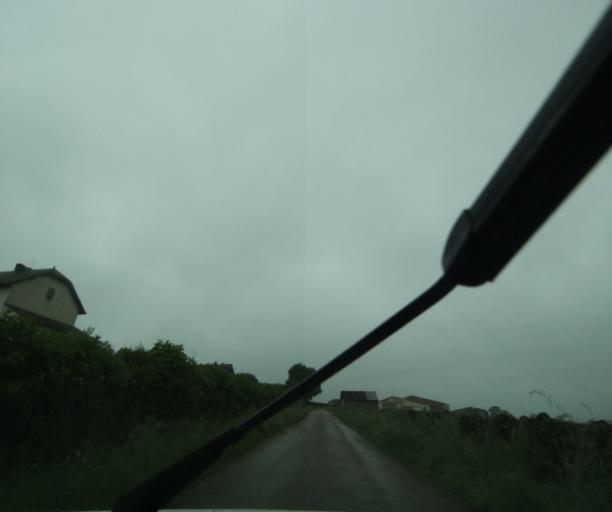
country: FR
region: Bourgogne
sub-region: Departement de Saone-et-Loire
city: Charolles
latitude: 46.3914
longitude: 4.2933
